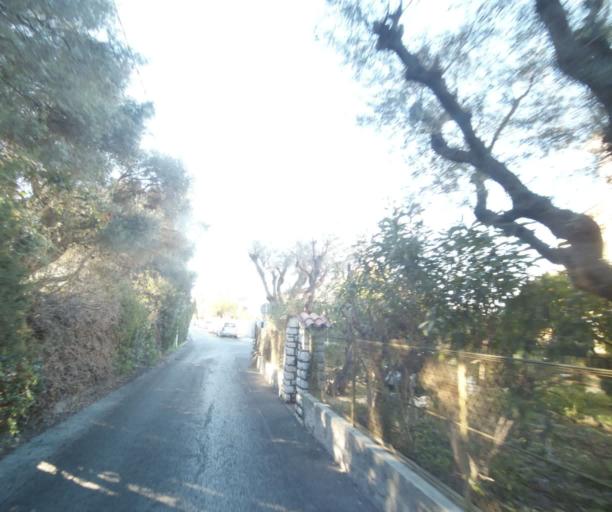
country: FR
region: Provence-Alpes-Cote d'Azur
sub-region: Departement des Alpes-Maritimes
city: Antibes
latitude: 43.5823
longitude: 7.1025
